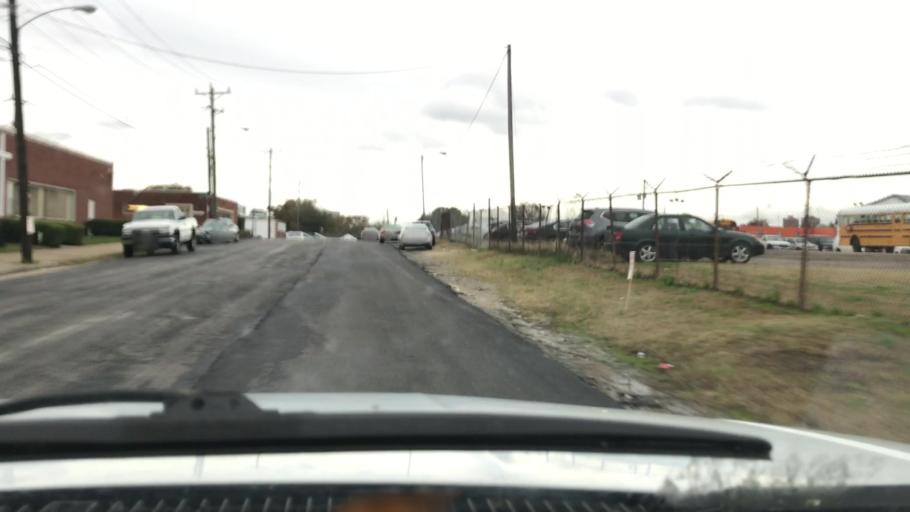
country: US
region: Virginia
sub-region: City of Richmond
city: Richmond
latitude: 37.5614
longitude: -77.4409
